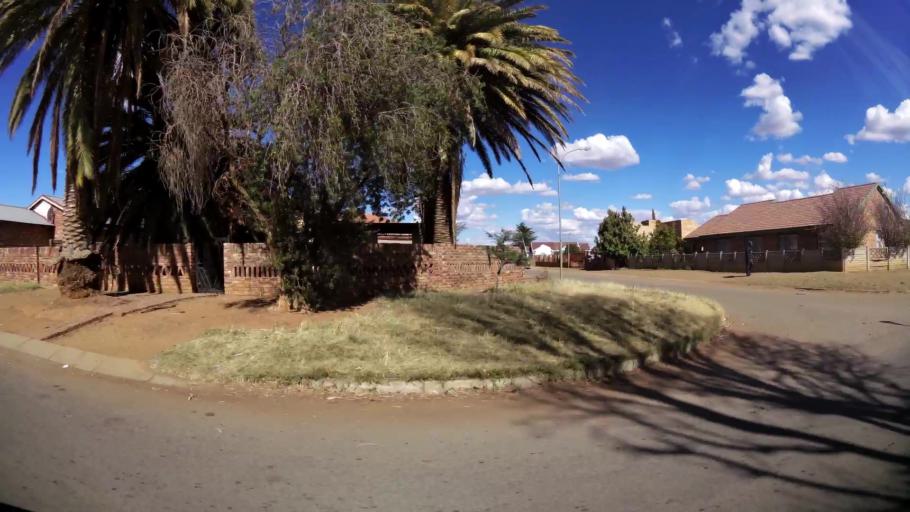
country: ZA
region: North-West
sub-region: Dr Kenneth Kaunda District Municipality
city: Klerksdorp
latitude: -26.8725
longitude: 26.5830
